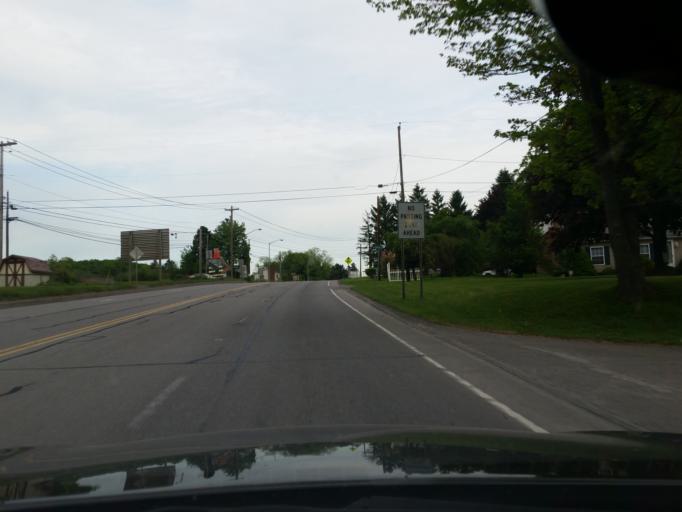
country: US
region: Pennsylvania
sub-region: Elk County
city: Ridgway
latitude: 41.4101
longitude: -78.7104
